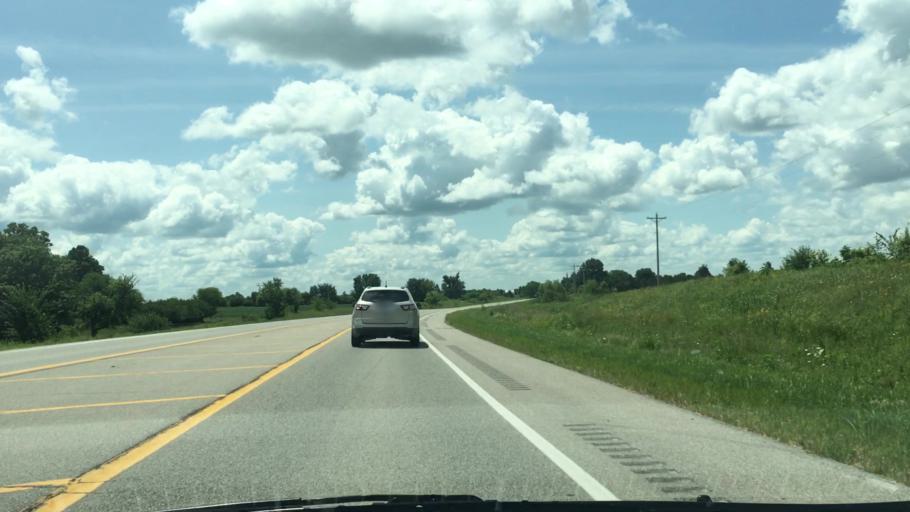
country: US
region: Iowa
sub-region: Johnson County
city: Solon
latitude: 41.7368
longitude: -91.4744
